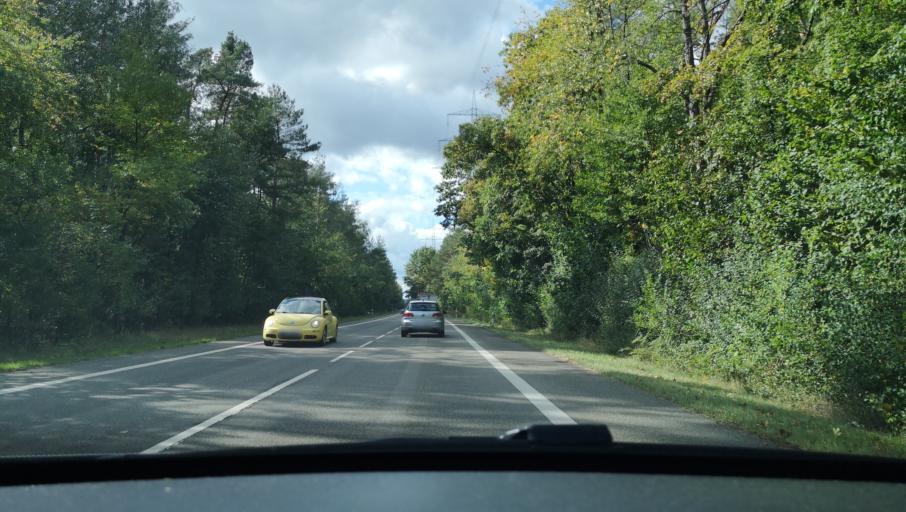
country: DE
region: Hesse
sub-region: Regierungsbezirk Darmstadt
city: Dietzenbach
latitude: 50.0114
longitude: 8.8243
